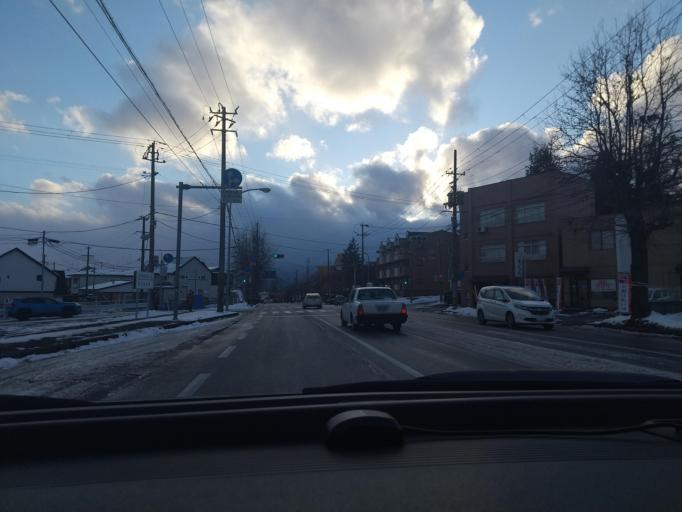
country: JP
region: Iwate
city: Morioka-shi
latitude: 39.7263
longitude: 141.1381
